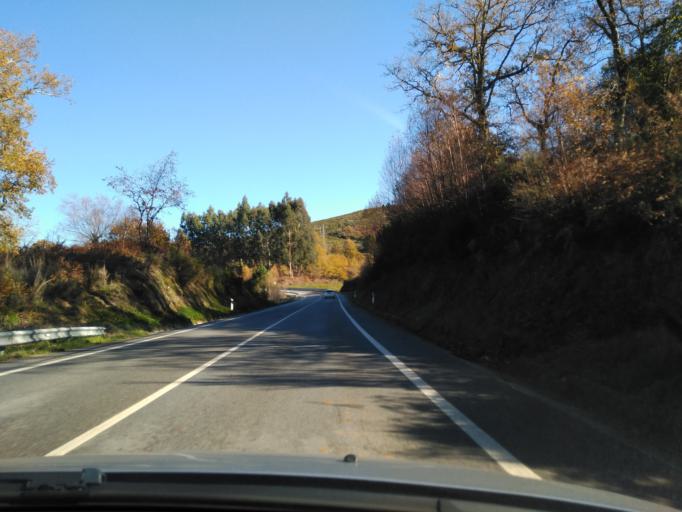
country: PT
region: Vila Real
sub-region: Montalegre
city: Montalegre
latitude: 41.7125
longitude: -7.8995
